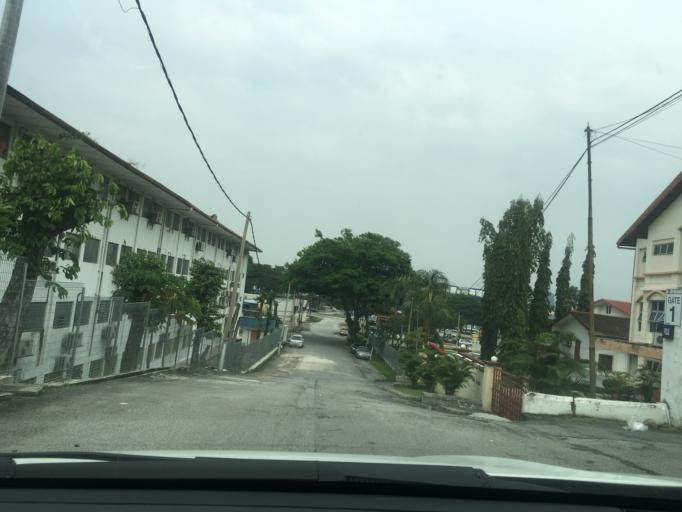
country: MY
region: Selangor
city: Klang
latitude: 3.0414
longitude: 101.4452
